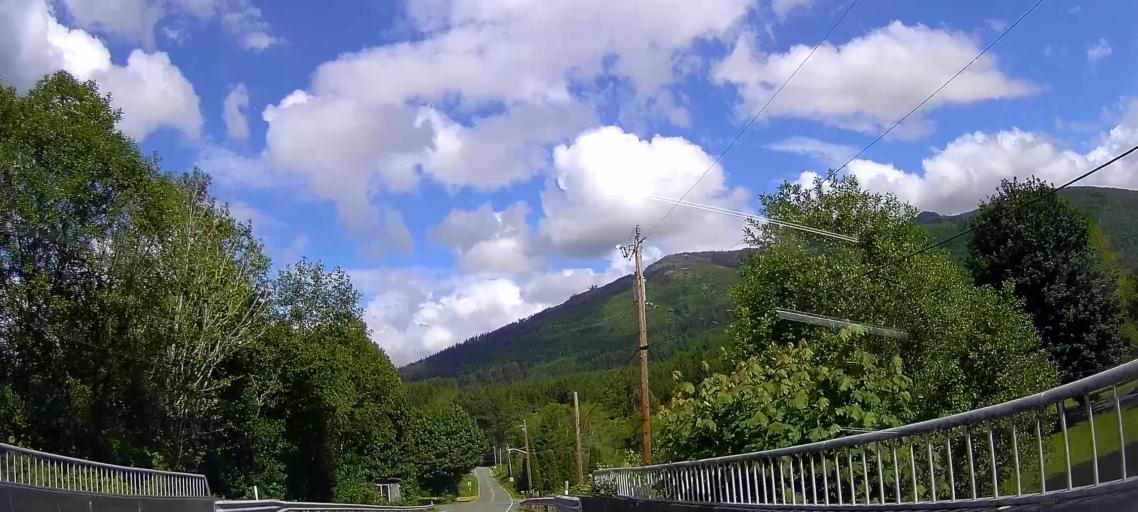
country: US
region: Washington
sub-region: Skagit County
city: Sedro-Woolley
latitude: 48.6531
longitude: -122.2095
